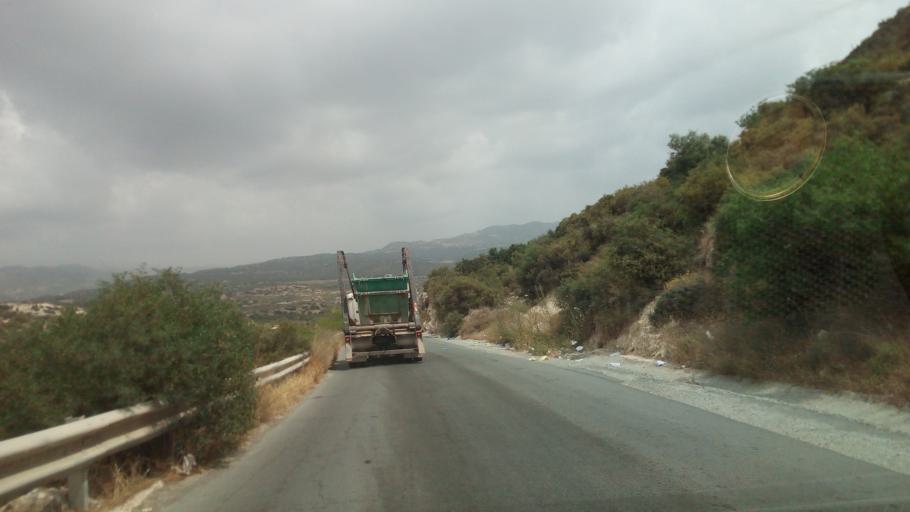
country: CY
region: Limassol
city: Pano Polemidia
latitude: 34.7520
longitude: 32.9536
